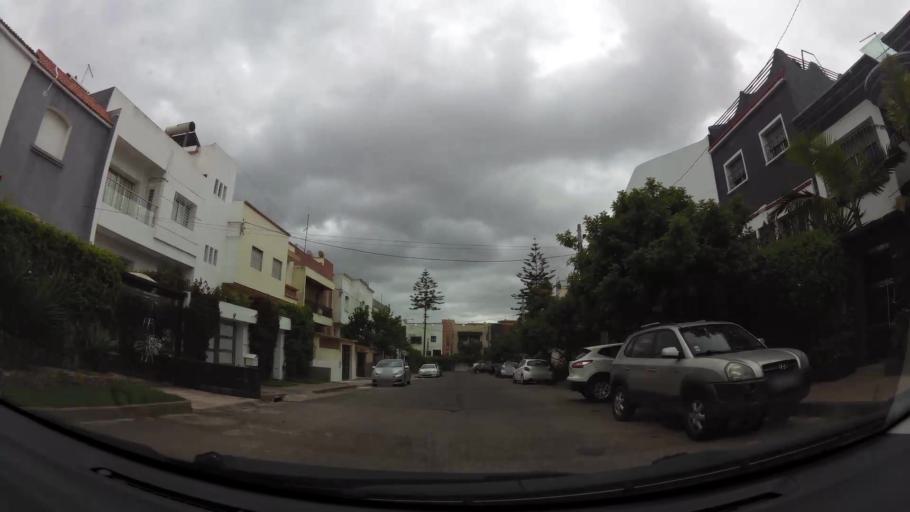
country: MA
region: Grand Casablanca
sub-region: Casablanca
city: Casablanca
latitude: 33.5747
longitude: -7.6706
